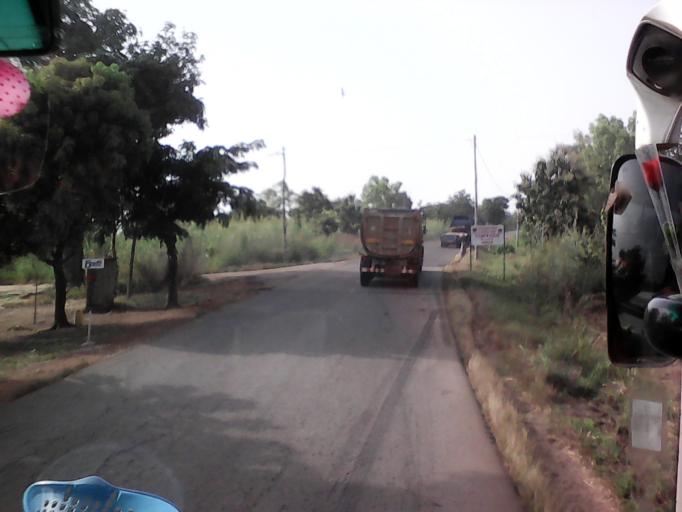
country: TG
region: Kara
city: Kara
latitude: 9.4633
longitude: 1.2164
